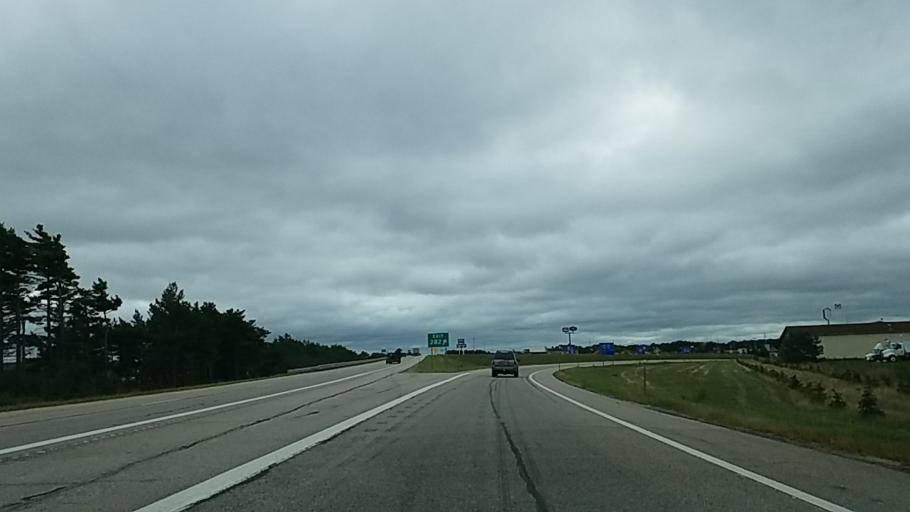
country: US
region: Michigan
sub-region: Otsego County
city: Gaylord
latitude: 45.0315
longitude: -84.6897
